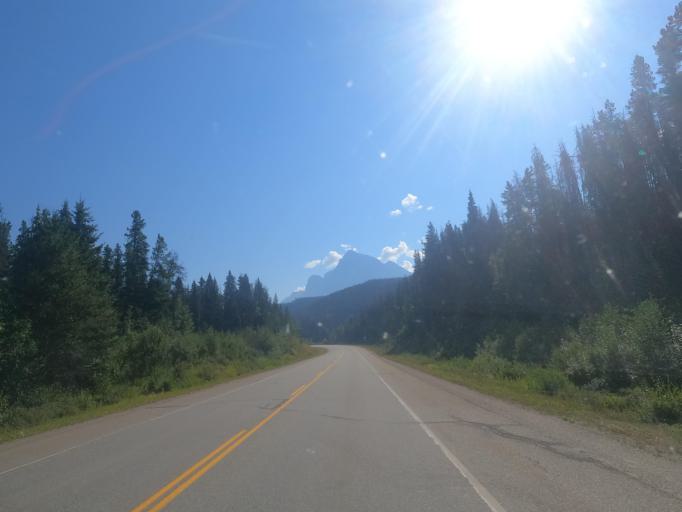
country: CA
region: Alberta
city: Jasper Park Lodge
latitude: 52.8491
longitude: -118.5806
